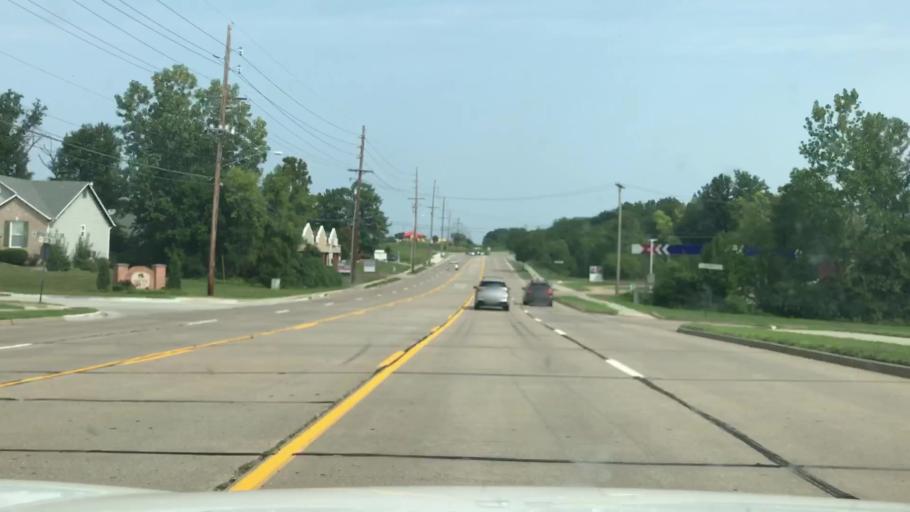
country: US
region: Missouri
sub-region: Saint Charles County
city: Dardenne Prairie
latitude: 38.7947
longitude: -90.7360
